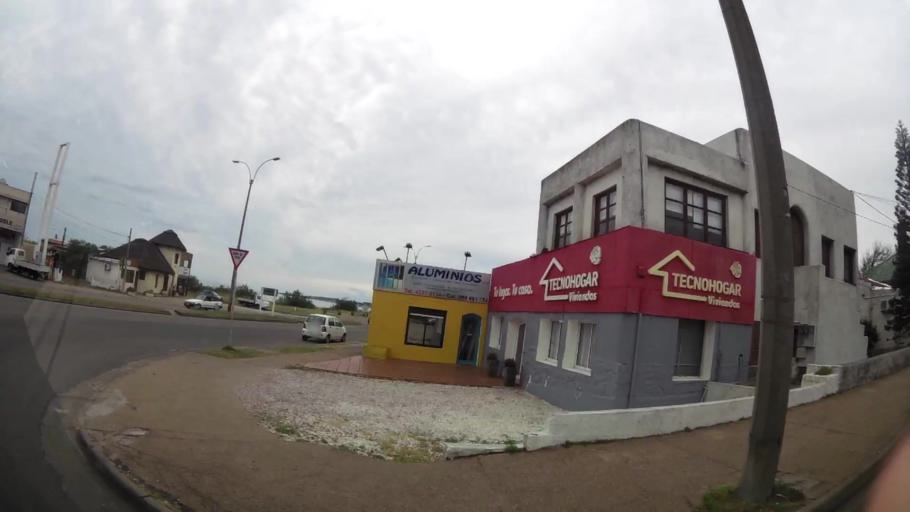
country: UY
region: Maldonado
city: Maldonado
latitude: -34.9191
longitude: -54.9717
